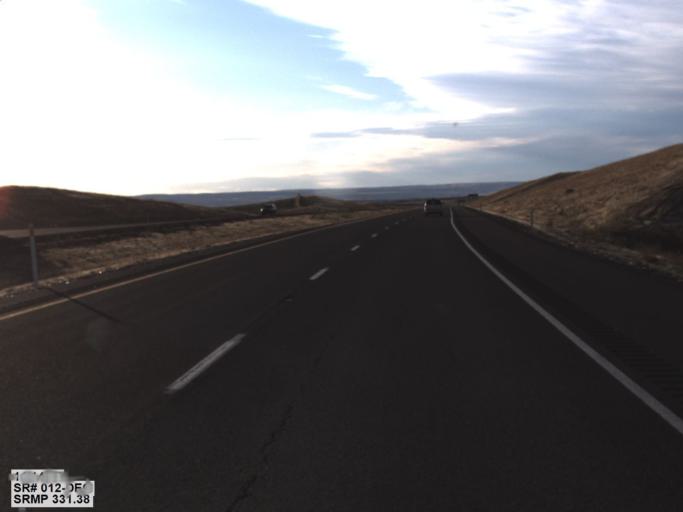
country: US
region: Washington
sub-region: Walla Walla County
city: Garrett
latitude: 46.0567
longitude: -118.4438
